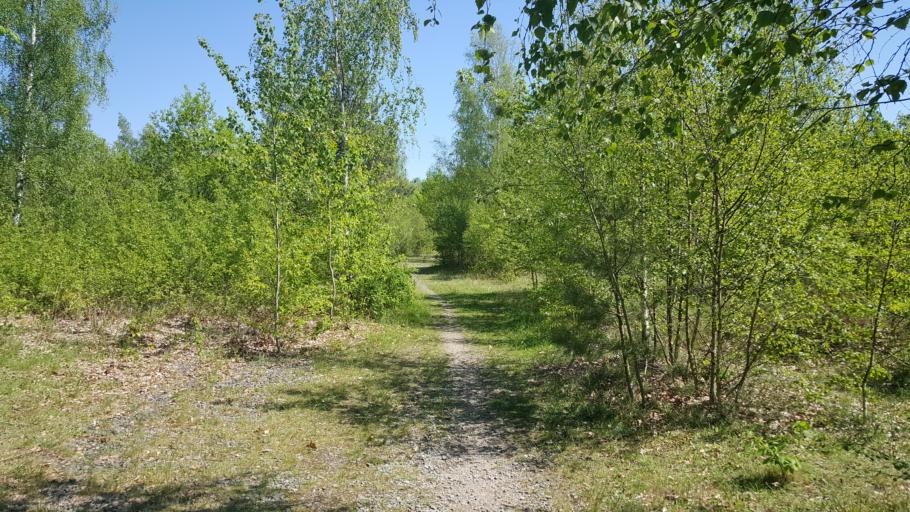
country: DE
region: Saxony
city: Albertstadt
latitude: 51.0985
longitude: 13.7484
